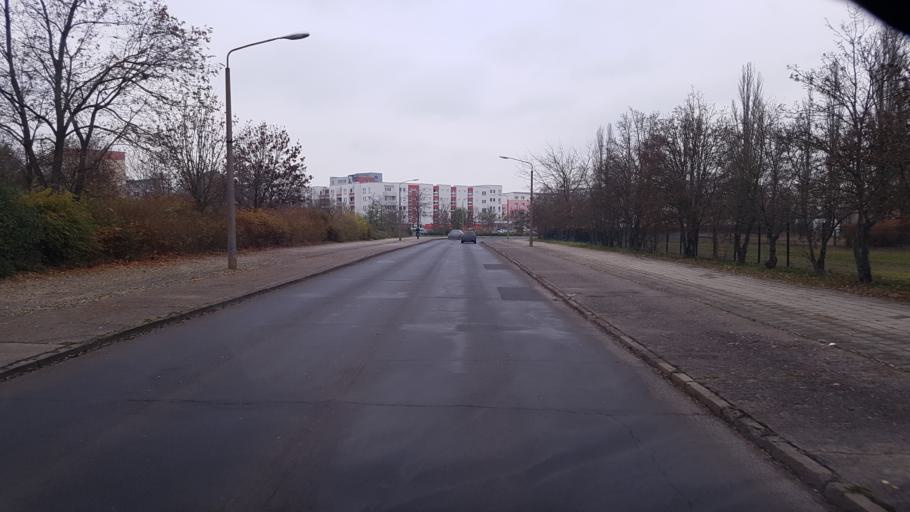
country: DE
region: Brandenburg
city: Eisenhuettenstadt
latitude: 52.1371
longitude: 14.6486
